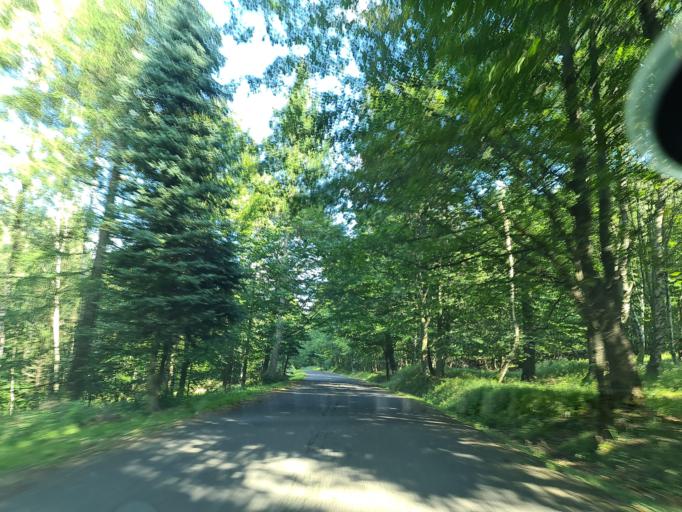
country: CZ
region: Ustecky
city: Horni Jiretin
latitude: 50.6098
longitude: 13.5370
